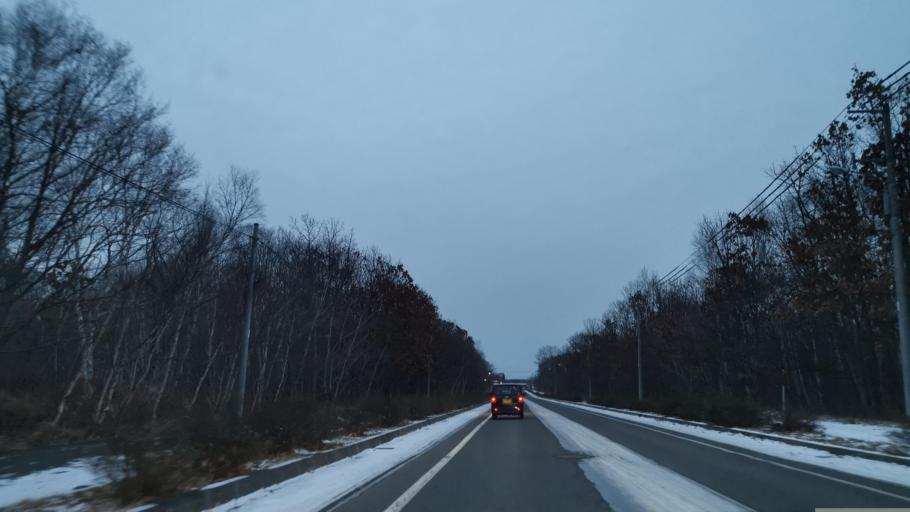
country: JP
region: Hokkaido
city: Chitose
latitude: 42.8170
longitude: 141.6693
